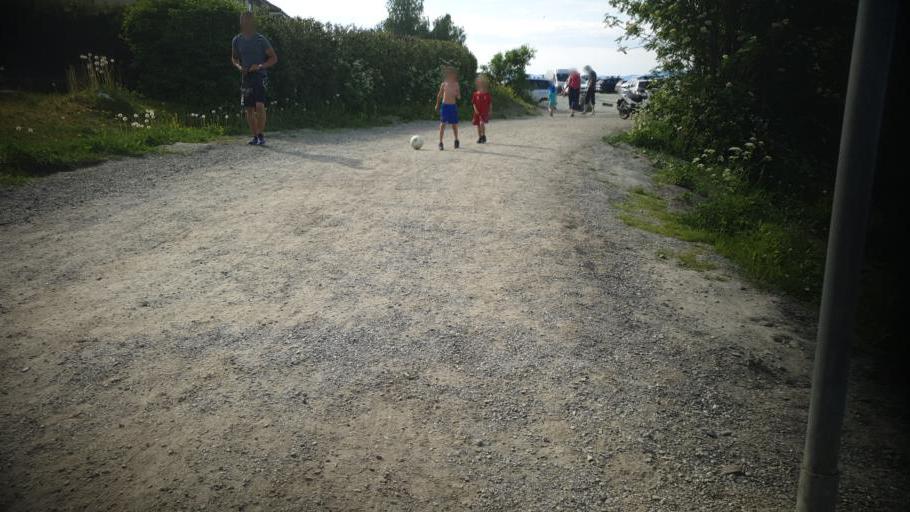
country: NO
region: Sor-Trondelag
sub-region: Malvik
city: Malvik
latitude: 63.4305
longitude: 10.5410
